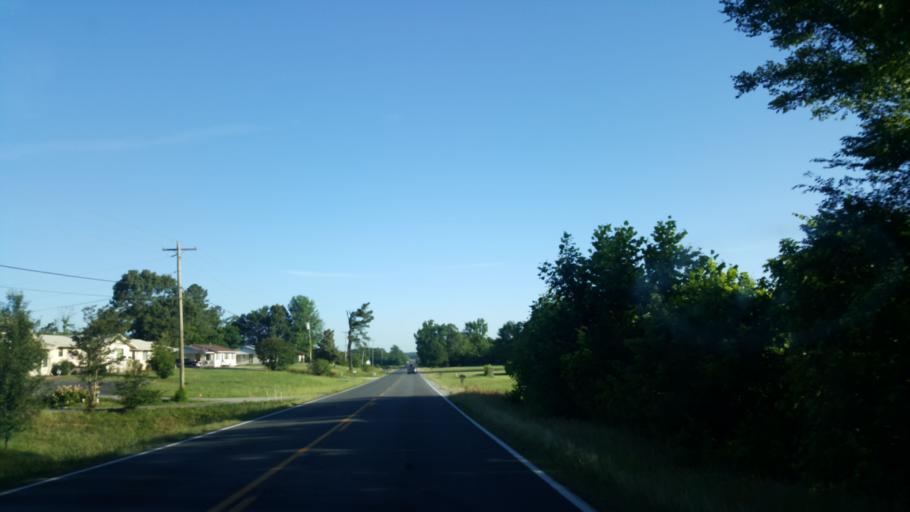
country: US
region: Tennessee
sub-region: Henderson County
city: Lexington
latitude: 35.6041
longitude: -88.3933
